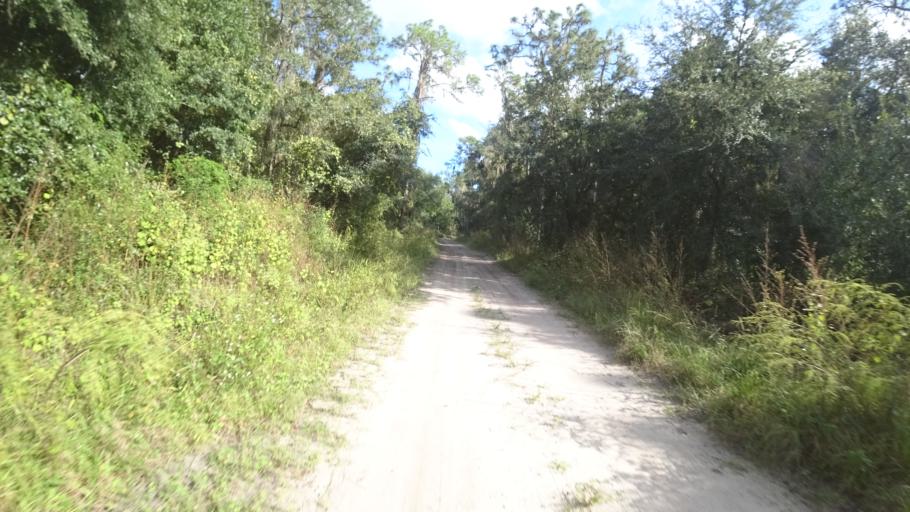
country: US
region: Florida
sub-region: DeSoto County
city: Arcadia
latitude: 27.3519
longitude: -82.1165
